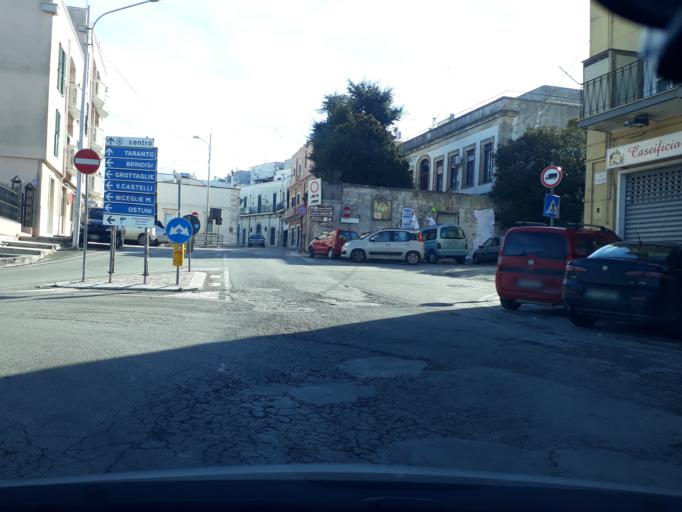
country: IT
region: Apulia
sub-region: Provincia di Taranto
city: Martina Franca
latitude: 40.7070
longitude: 17.3388
